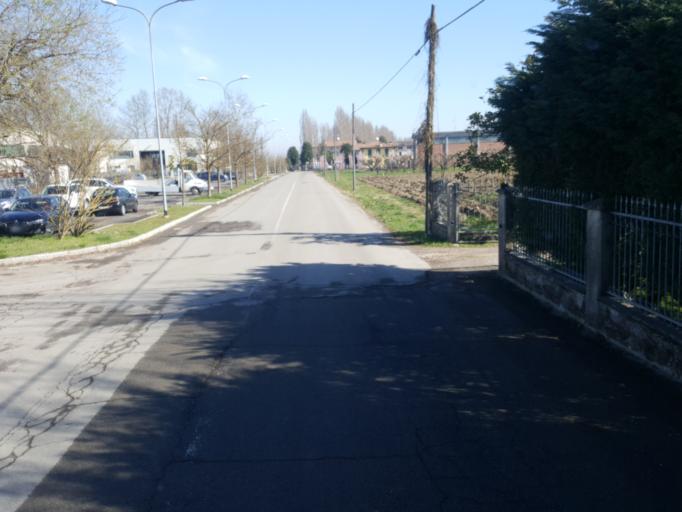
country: IT
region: Emilia-Romagna
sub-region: Provincia di Modena
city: Solara
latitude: 44.7739
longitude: 11.0908
